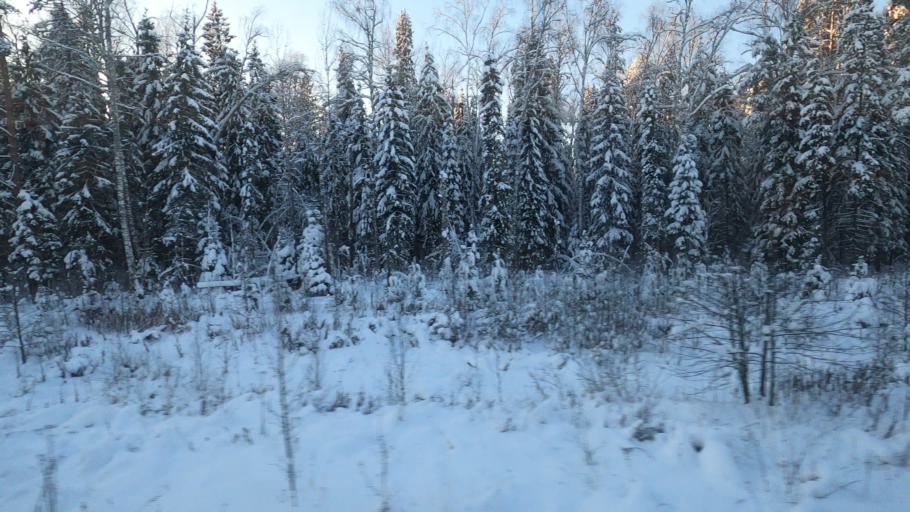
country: RU
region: Moskovskaya
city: Zhukovka
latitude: 56.4994
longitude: 37.5526
